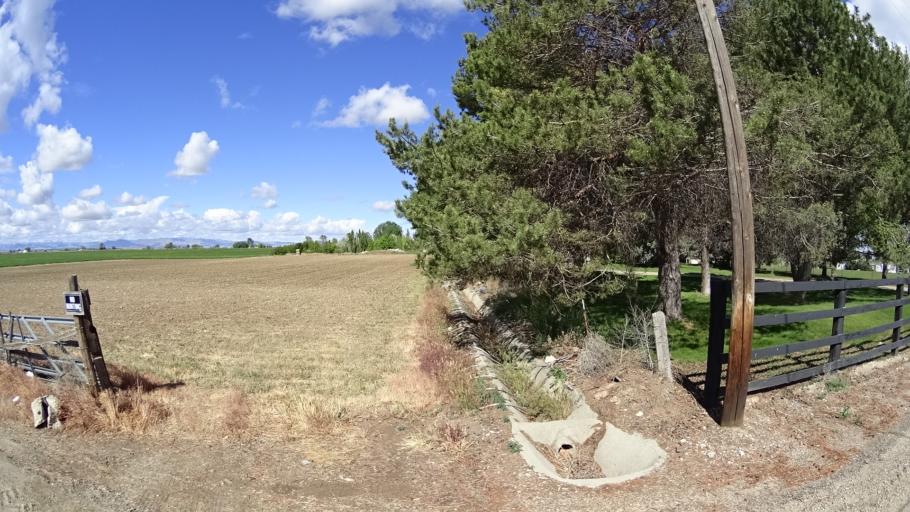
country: US
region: Idaho
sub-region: Ada County
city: Kuna
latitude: 43.4957
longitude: -116.4537
